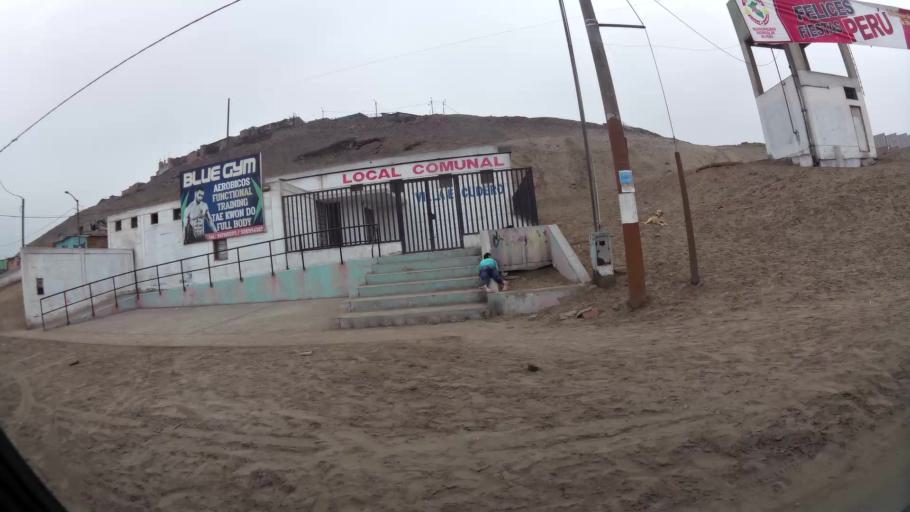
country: PE
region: Lima
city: Ventanilla
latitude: -11.8456
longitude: -77.1144
